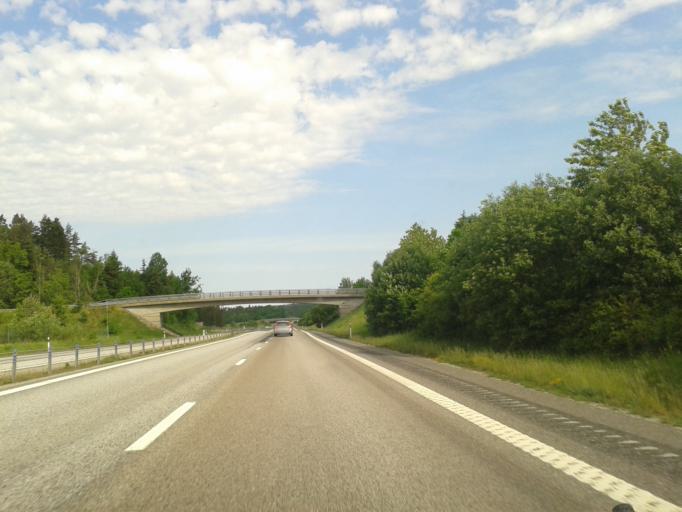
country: SE
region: Vaestra Goetaland
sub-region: Munkedals Kommun
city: Munkedal
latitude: 58.5303
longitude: 11.5396
